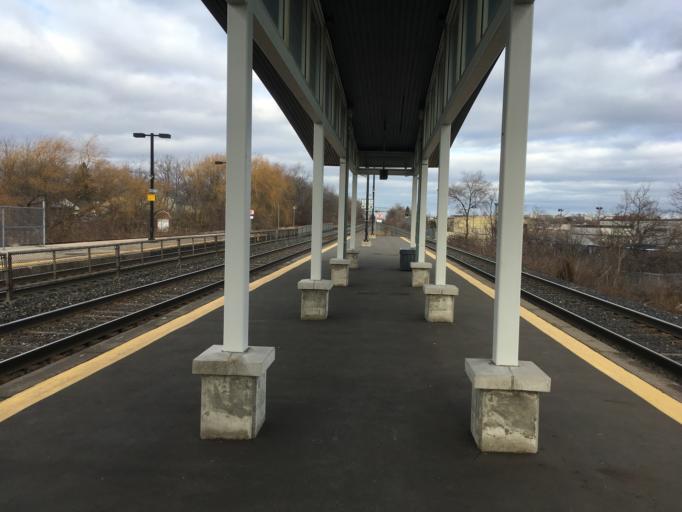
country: CA
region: Ontario
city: Burlington
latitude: 43.3416
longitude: -79.8084
